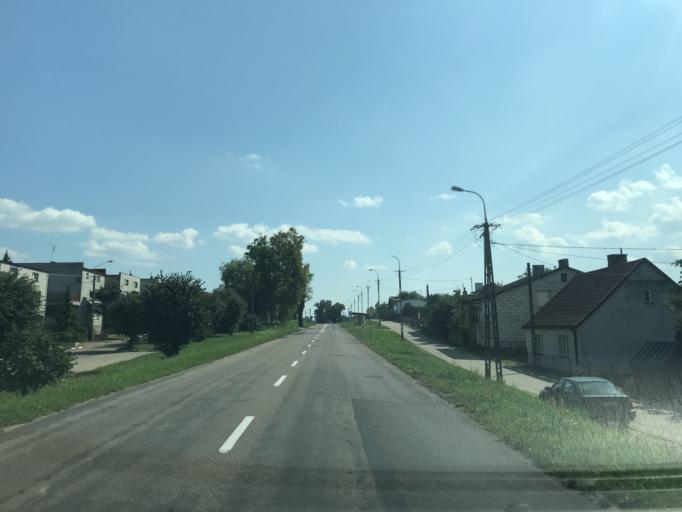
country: PL
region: Warmian-Masurian Voivodeship
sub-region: Powiat dzialdowski
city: Lidzbark
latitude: 53.2508
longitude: 19.8230
